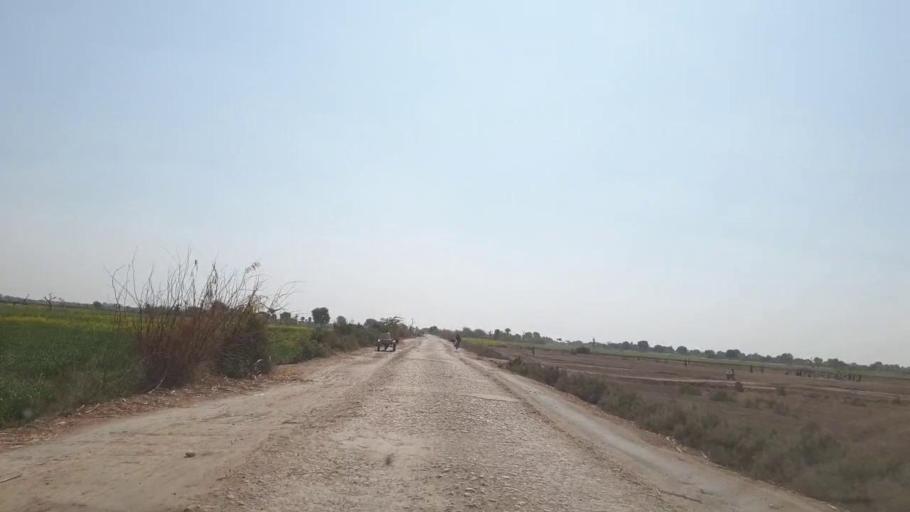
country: PK
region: Sindh
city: Mirpur Khas
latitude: 25.7413
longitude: 69.0823
